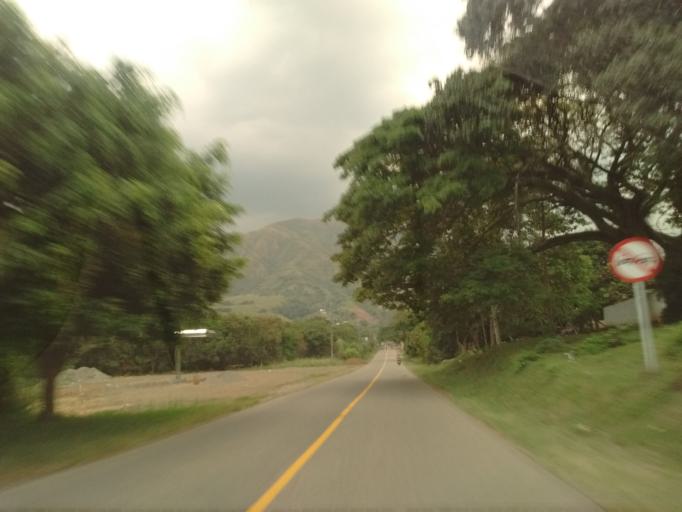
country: CO
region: Cauca
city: Caloto
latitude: 3.0657
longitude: -76.3586
